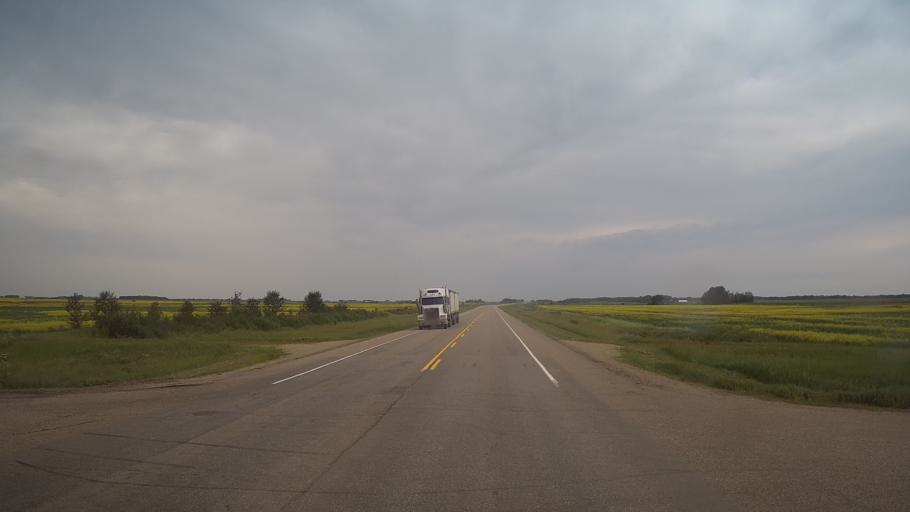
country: CA
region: Saskatchewan
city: Langham
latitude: 52.1283
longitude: -107.2411
